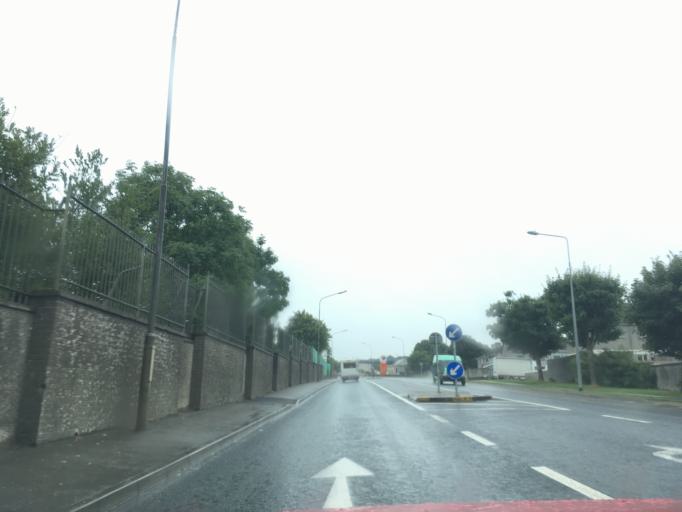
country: IE
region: Leinster
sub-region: Loch Garman
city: New Ross
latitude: 52.3941
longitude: -6.9341
